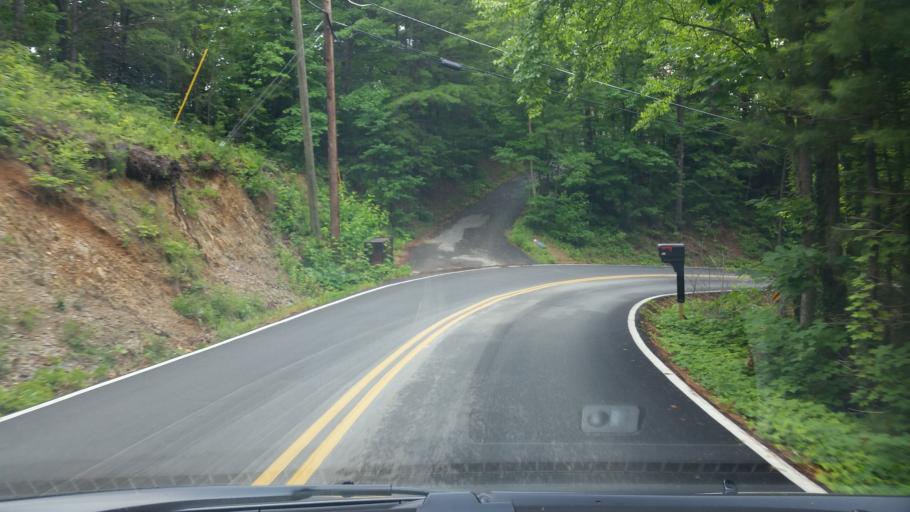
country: US
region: Tennessee
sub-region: Sevier County
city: Gatlinburg
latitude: 35.7125
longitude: -83.5451
